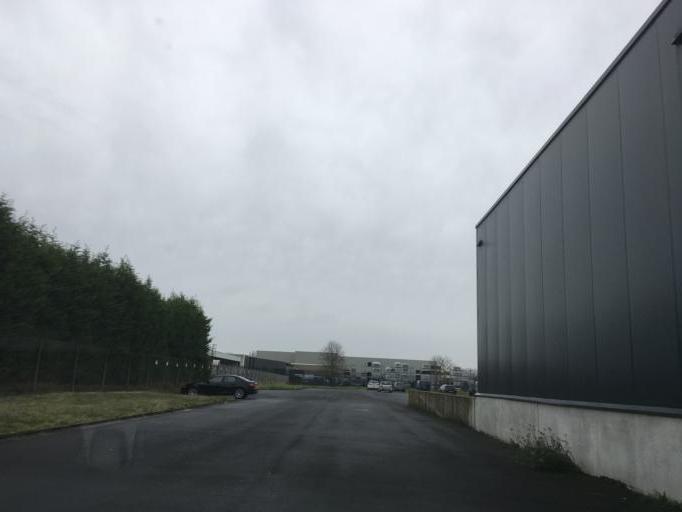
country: BE
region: Flanders
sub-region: Provincie West-Vlaanderen
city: Roeselare
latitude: 50.9745
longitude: 3.1253
